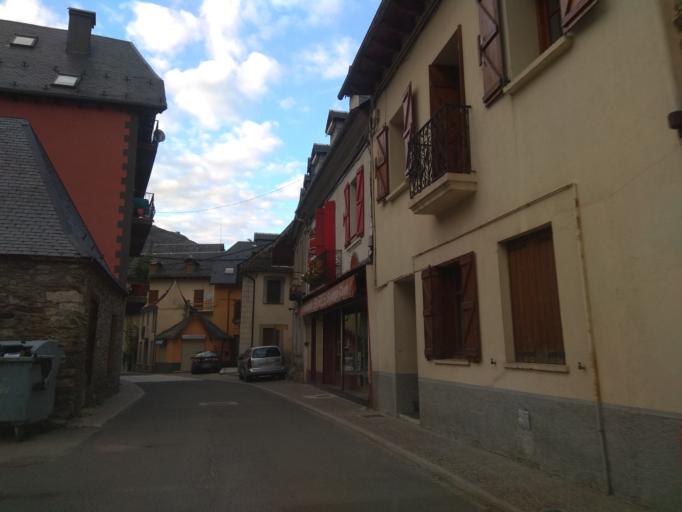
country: ES
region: Catalonia
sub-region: Provincia de Lleida
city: Les
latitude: 42.8095
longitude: 0.7112
